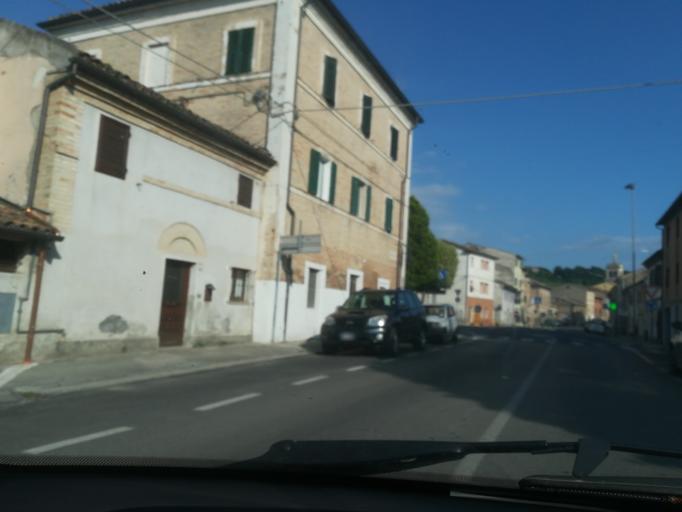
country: IT
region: The Marches
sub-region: Provincia di Macerata
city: Villa Potenza
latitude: 43.3240
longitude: 13.4254
